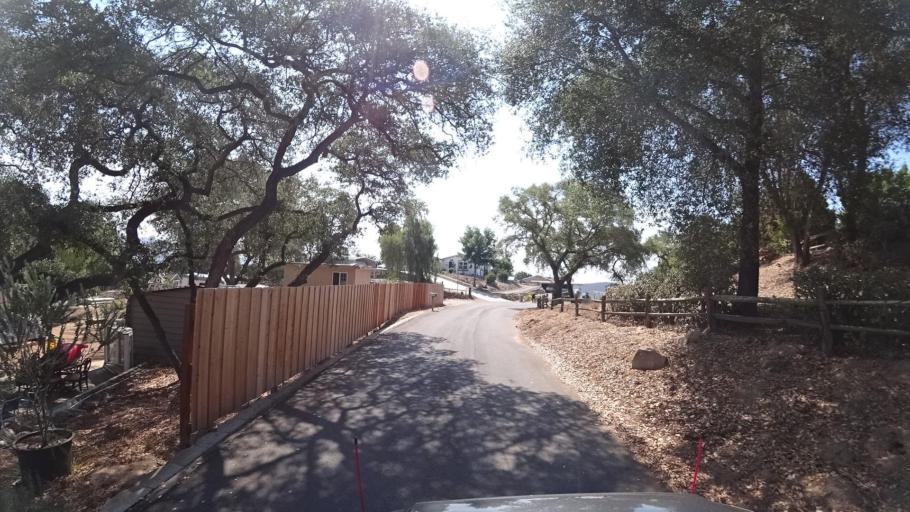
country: US
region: California
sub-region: San Diego County
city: Hidden Meadows
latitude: 33.1793
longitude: -117.1063
